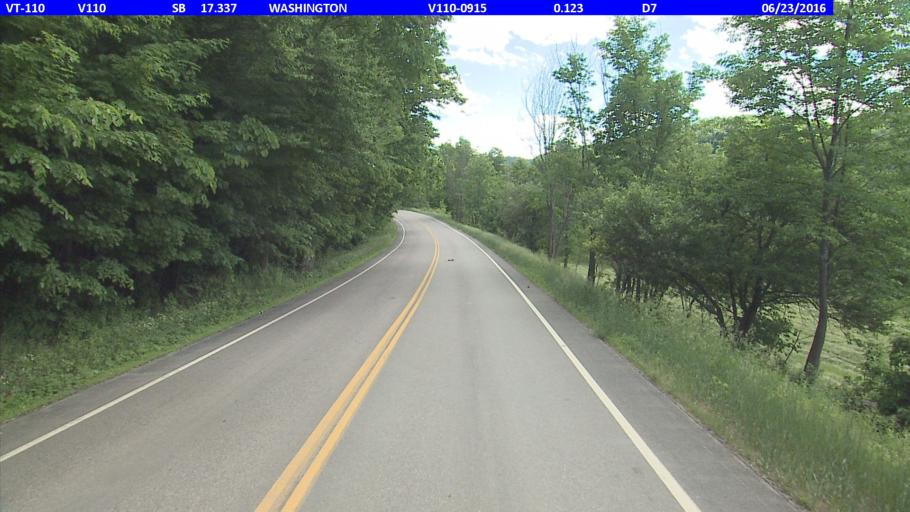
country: US
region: Vermont
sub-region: Orange County
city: Chelsea
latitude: 44.0424
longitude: -72.4744
